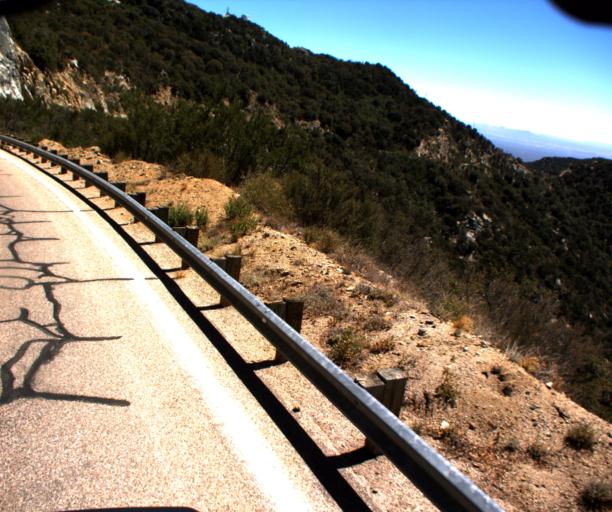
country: US
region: Arizona
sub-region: Pima County
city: Sells
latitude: 31.9635
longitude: -111.6015
